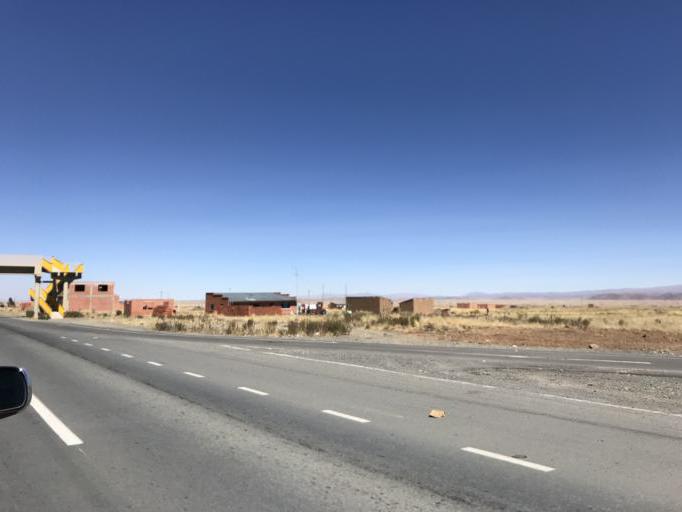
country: BO
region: La Paz
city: Batallas
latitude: -16.3695
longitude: -68.3867
